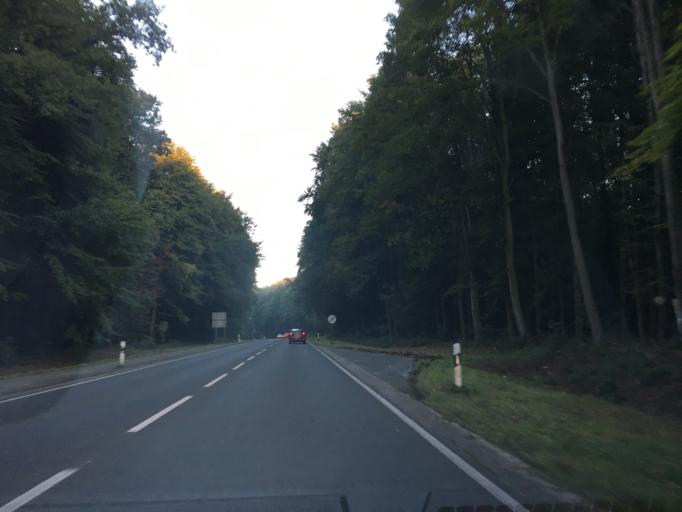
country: DE
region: North Rhine-Westphalia
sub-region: Regierungsbezirk Munster
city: Steinfurt
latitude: 52.1436
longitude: 7.3565
